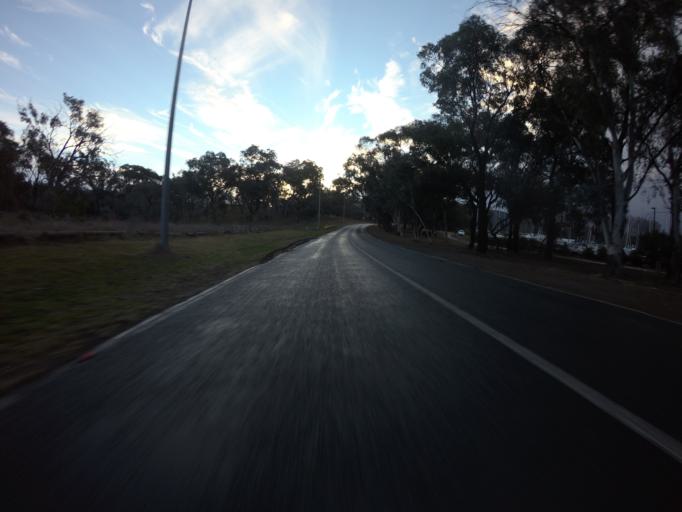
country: AU
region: Australian Capital Territory
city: Forrest
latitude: -35.3006
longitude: 149.1168
